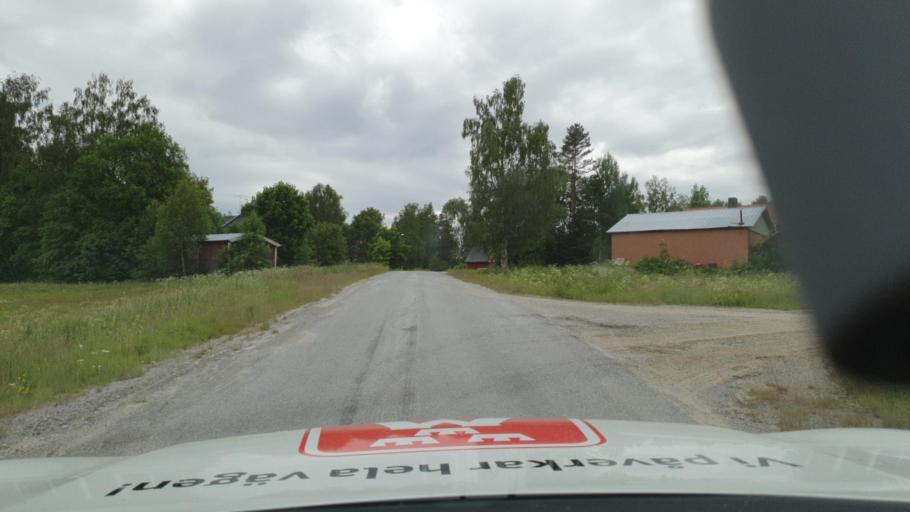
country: SE
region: Vaesterbotten
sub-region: Bjurholms Kommun
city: Bjurholm
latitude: 63.7642
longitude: 19.3127
